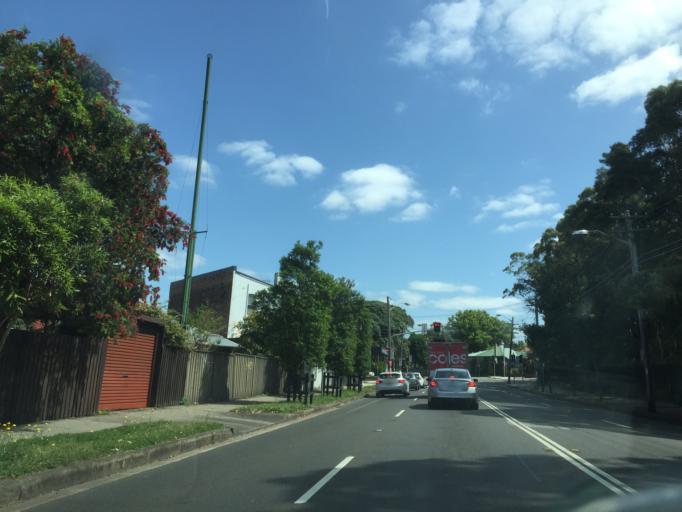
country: AU
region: New South Wales
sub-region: Marrickville
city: Marrickville
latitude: -33.9022
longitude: 151.1540
